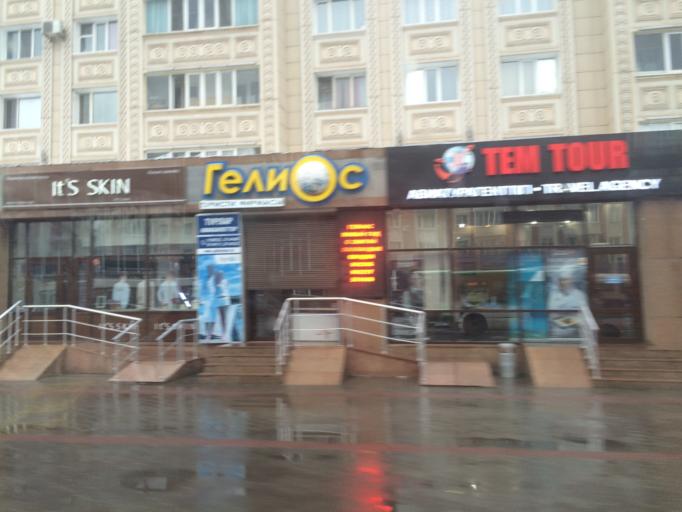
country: KZ
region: Astana Qalasy
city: Astana
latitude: 51.1596
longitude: 71.4287
